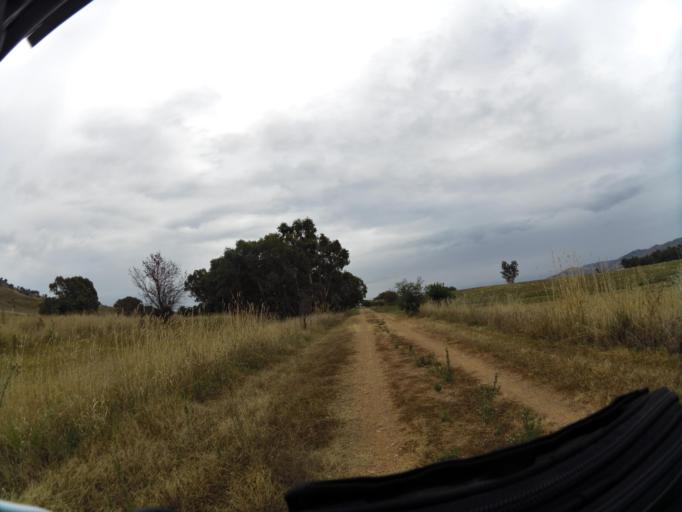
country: AU
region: New South Wales
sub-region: Albury Municipality
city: East Albury
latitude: -36.2137
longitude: 147.0565
